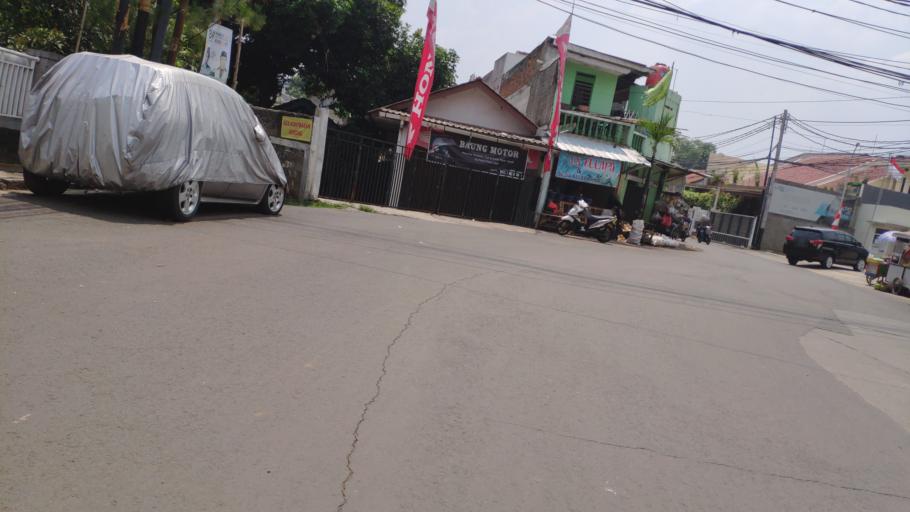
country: ID
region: Jakarta Raya
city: Jakarta
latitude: -6.3059
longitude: 106.8361
